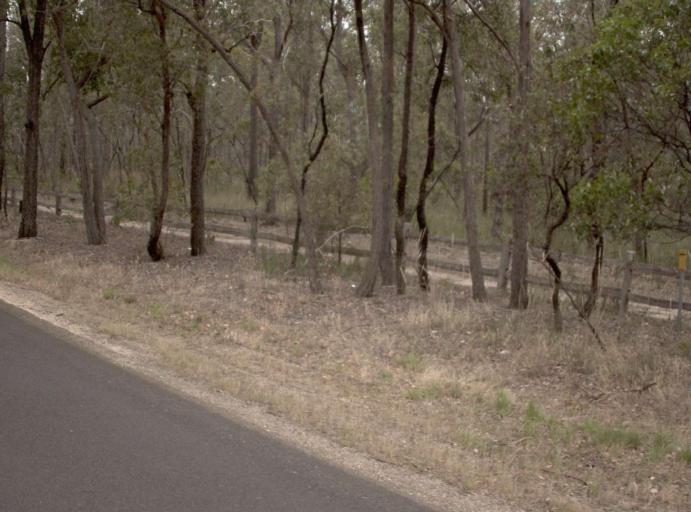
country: AU
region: Victoria
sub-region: Wellington
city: Heyfield
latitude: -37.9565
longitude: 146.7713
